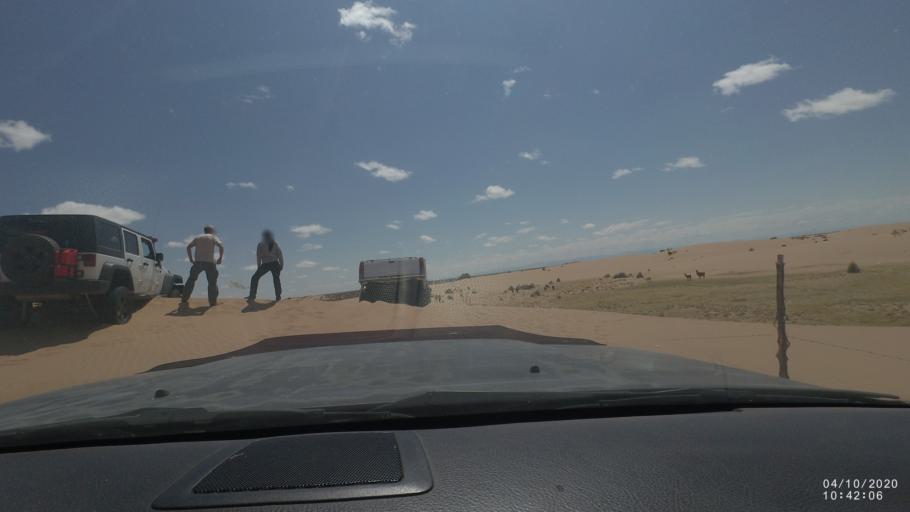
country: BO
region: Oruro
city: Poopo
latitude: -18.7044
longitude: -67.4712
